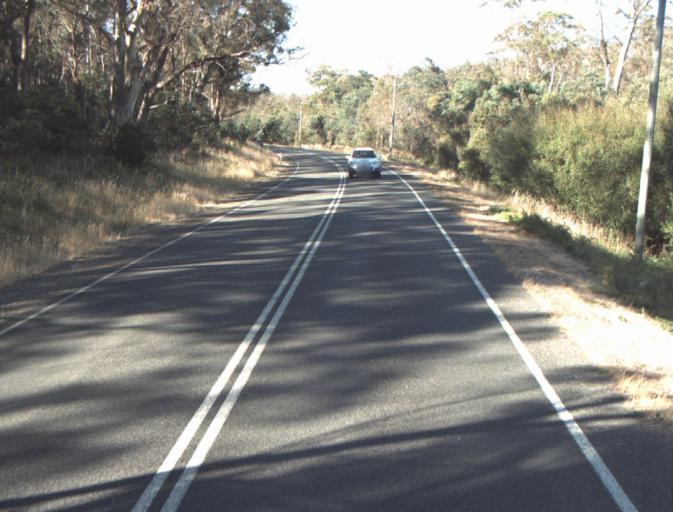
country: AU
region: Tasmania
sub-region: Launceston
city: Newstead
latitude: -41.4208
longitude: 147.2566
